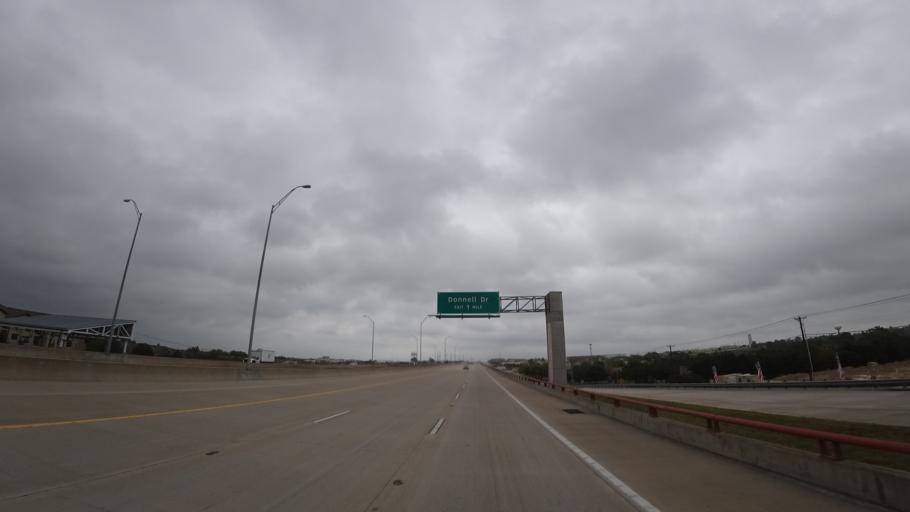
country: US
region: Texas
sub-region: Travis County
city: Windemere
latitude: 30.4839
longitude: -97.6548
